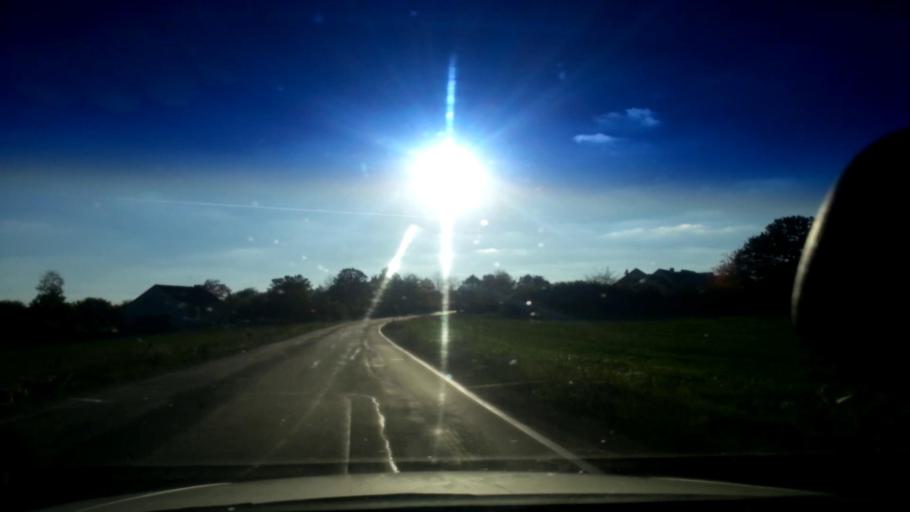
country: DE
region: Bavaria
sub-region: Upper Franconia
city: Rattelsdorf
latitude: 50.0184
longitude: 10.8987
